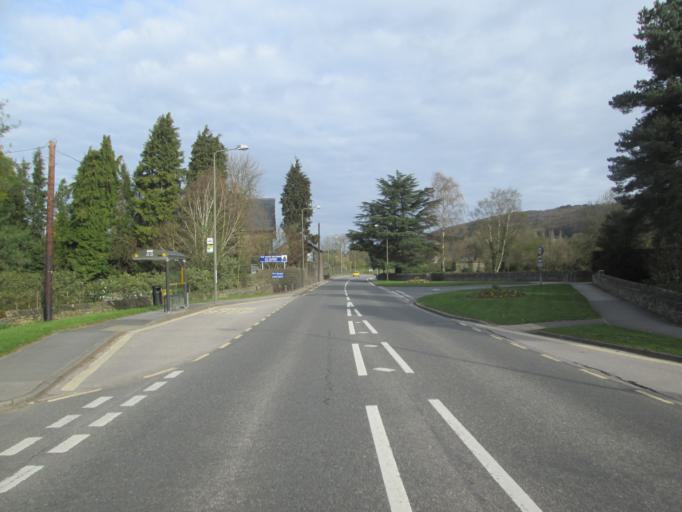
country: GB
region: England
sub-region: Derbyshire
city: Matlock
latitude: 53.1576
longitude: -1.5850
